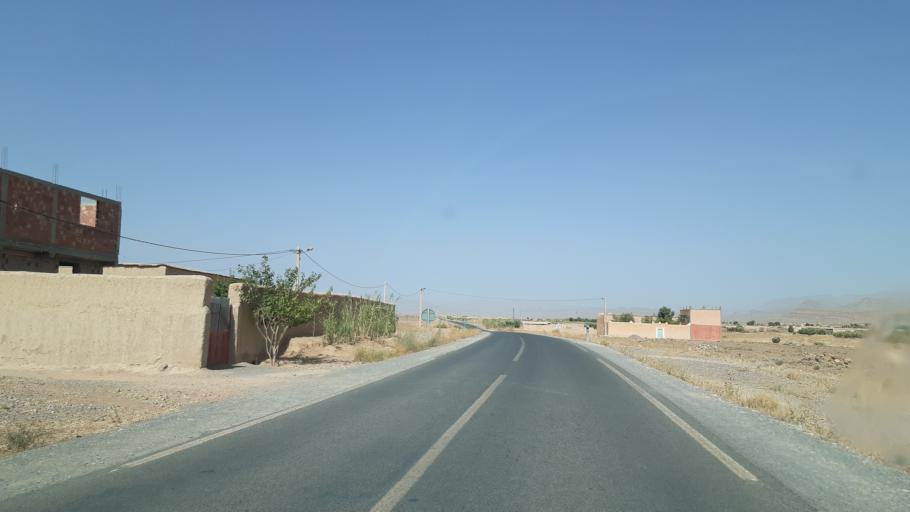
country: MA
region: Meknes-Tafilalet
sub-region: Errachidia
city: Amouguer
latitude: 32.2375
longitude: -4.6166
